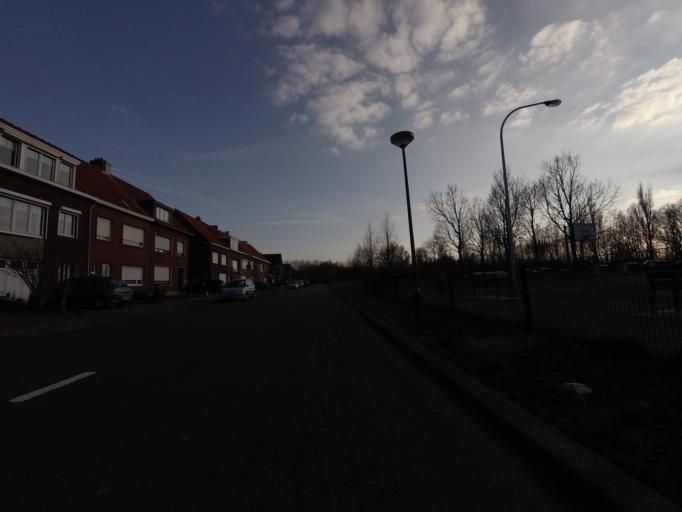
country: BE
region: Flanders
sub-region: Provincie Antwerpen
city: Kapellen
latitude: 51.2777
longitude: 4.4072
